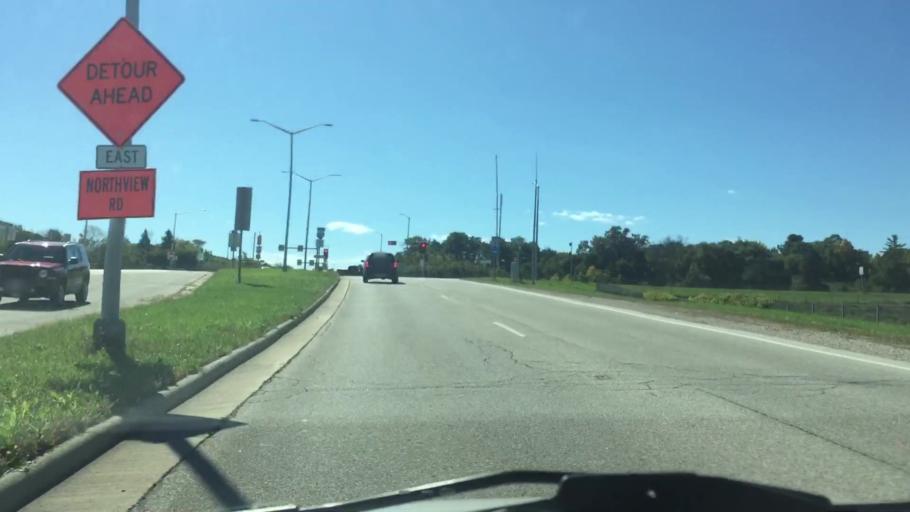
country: US
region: Wisconsin
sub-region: Waukesha County
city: Pewaukee
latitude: 43.0510
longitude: -88.2857
